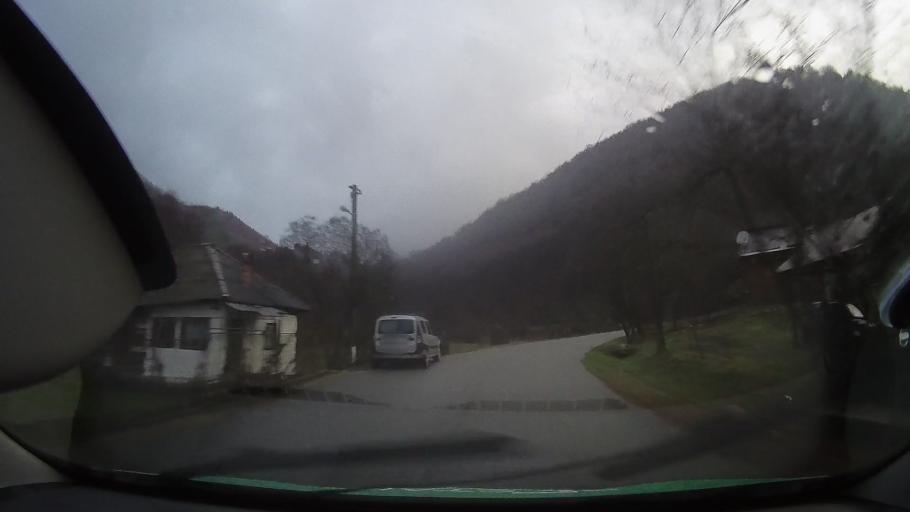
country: RO
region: Hunedoara
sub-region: Comuna Ribita
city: Ribita
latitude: 46.2767
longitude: 22.7411
